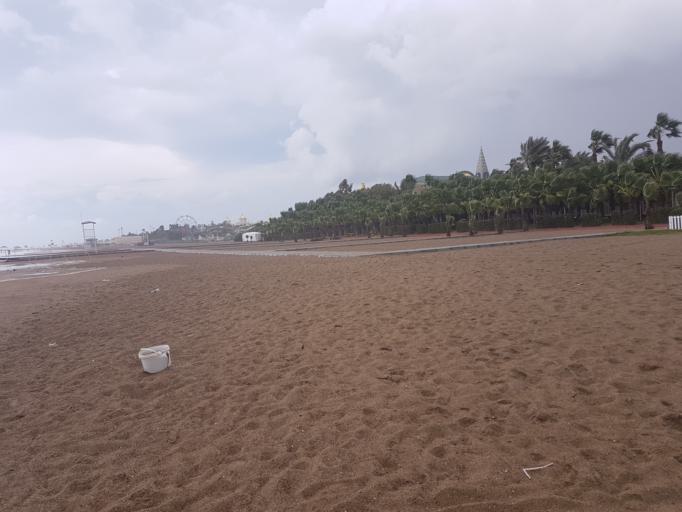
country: TR
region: Antalya
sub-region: Serik
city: Kumkoey
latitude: 36.8528
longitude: 30.8769
